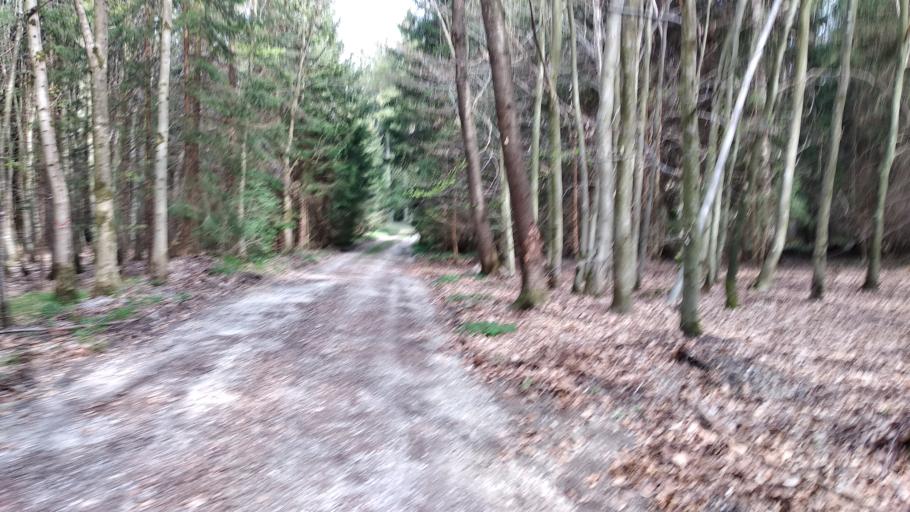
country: DE
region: Bavaria
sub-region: Swabia
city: Kronburg
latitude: 47.9002
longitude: 10.1488
